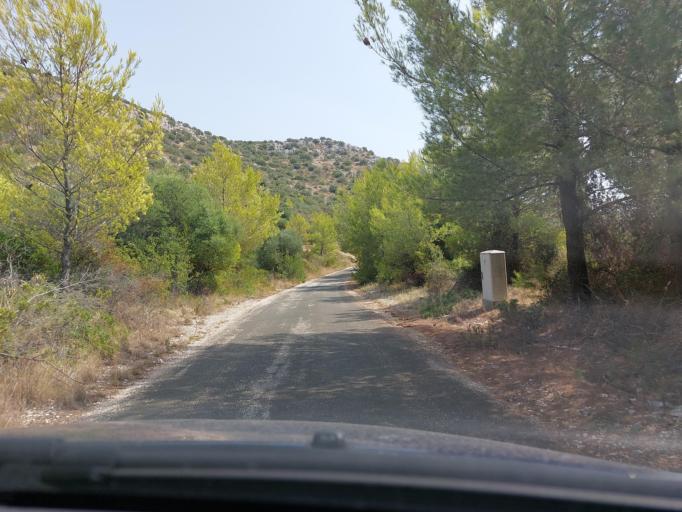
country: HR
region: Dubrovacko-Neretvanska
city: Smokvica
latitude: 42.7384
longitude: 16.8888
